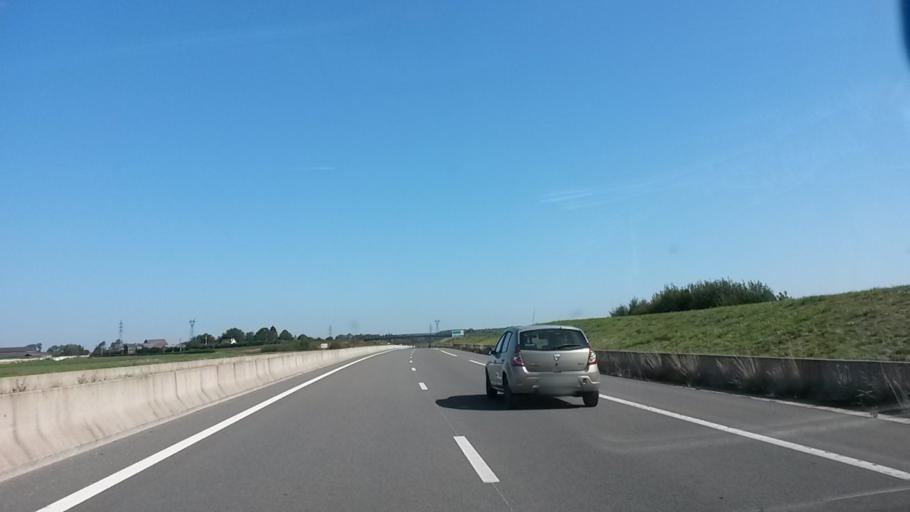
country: FR
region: Nord-Pas-de-Calais
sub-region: Departement du Nord
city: Louvroil
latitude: 50.2203
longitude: 3.9548
